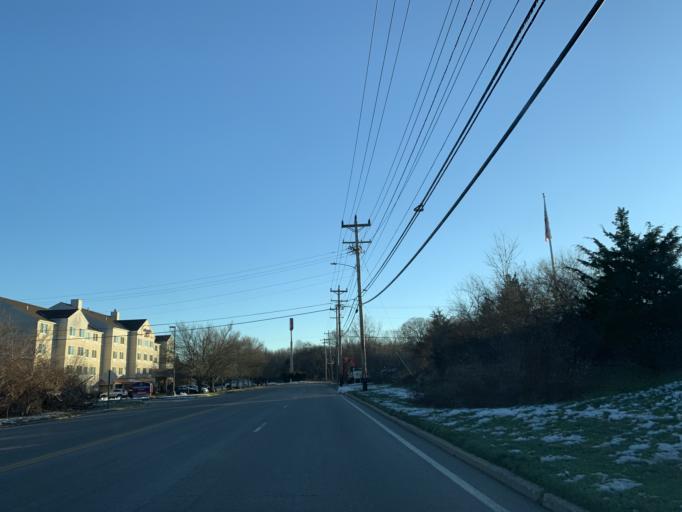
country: US
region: Rhode Island
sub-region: Kent County
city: West Warwick
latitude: 41.6695
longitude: -71.5042
